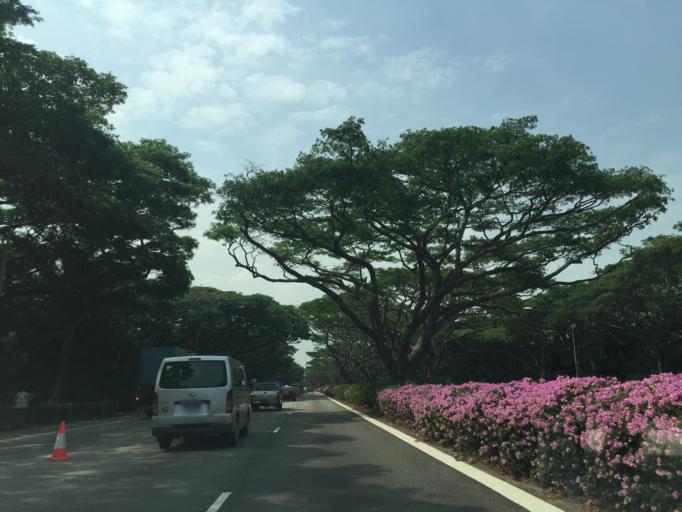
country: SG
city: Singapore
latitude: 1.3310
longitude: 103.9760
